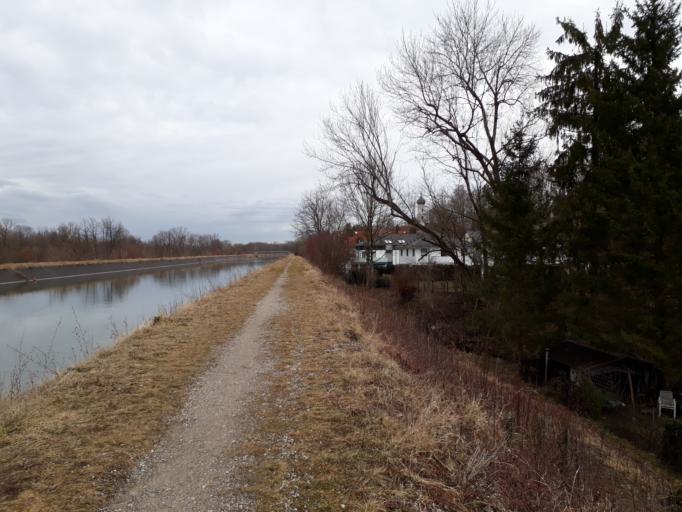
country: DE
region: Bavaria
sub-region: Upper Bavaria
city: Unterfoehring
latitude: 48.1898
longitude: 11.6355
